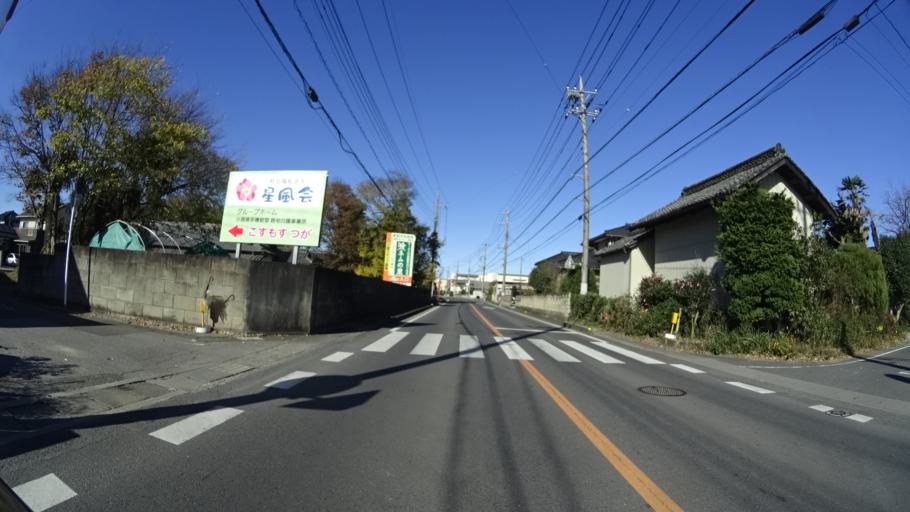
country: JP
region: Tochigi
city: Tochigi
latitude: 36.4253
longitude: 139.7495
